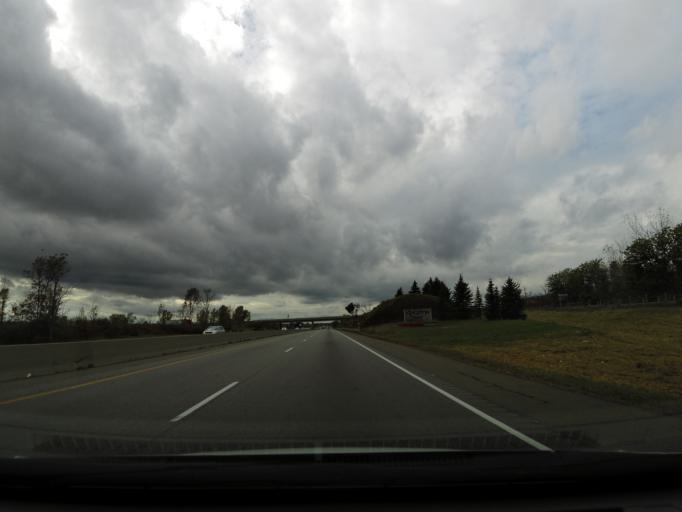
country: CA
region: Ontario
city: Gananoque
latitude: 44.3234
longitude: -76.3281
